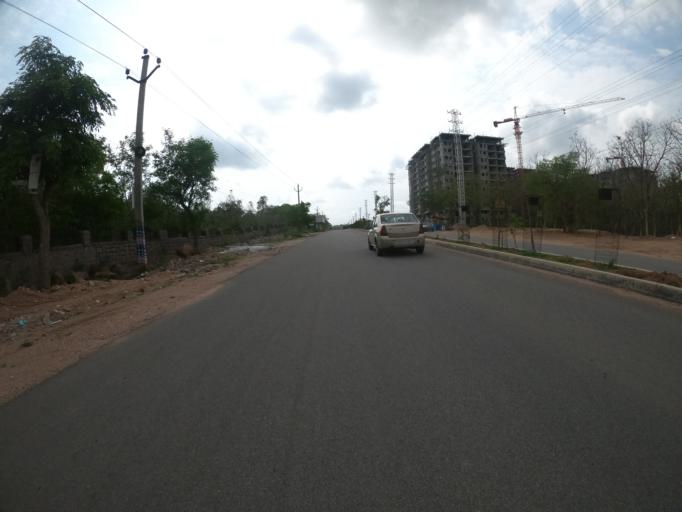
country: IN
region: Telangana
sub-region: Medak
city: Serilingampalle
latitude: 17.3914
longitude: 78.3237
